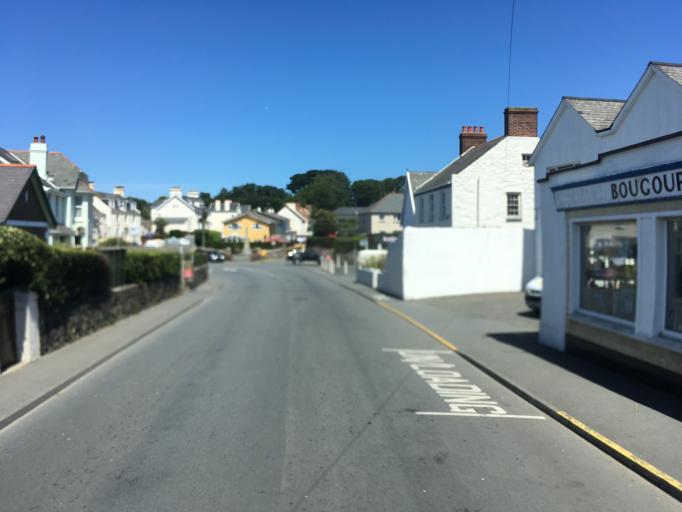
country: GG
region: St Peter Port
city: Saint Peter Port
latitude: 49.4860
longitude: -2.5190
